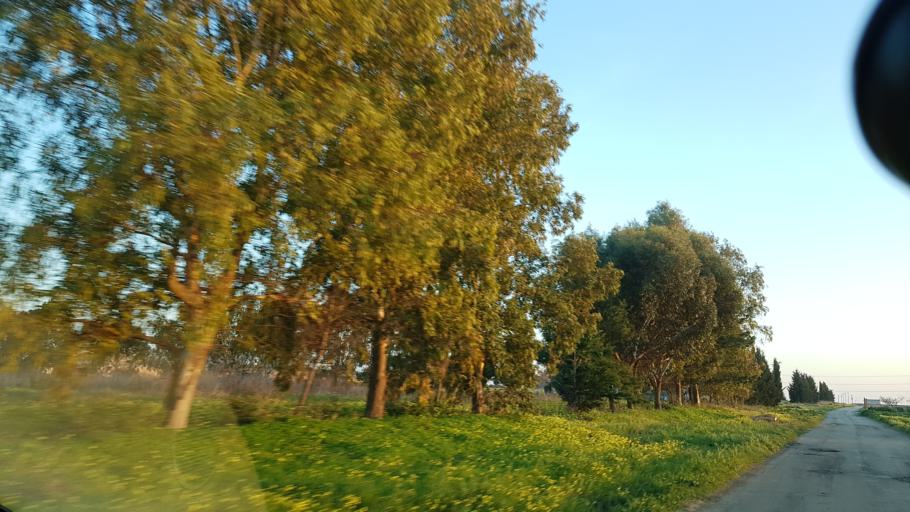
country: IT
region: Apulia
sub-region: Provincia di Brindisi
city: La Rosa
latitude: 40.6012
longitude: 17.9516
